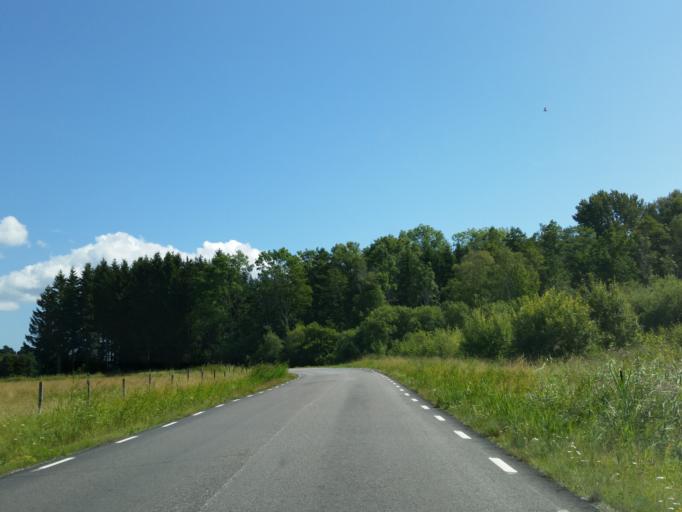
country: SE
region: Stockholm
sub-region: Sodertalje Kommun
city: Pershagen
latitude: 59.0479
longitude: 17.6811
